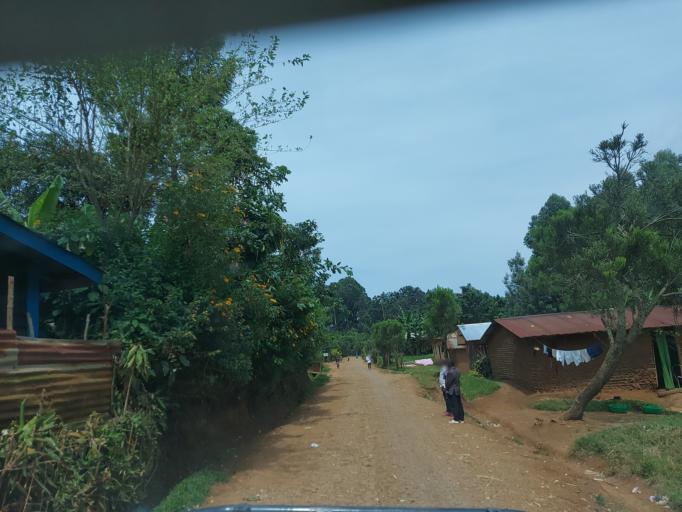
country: RW
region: Western Province
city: Cyangugu
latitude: -2.2343
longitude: 28.8518
